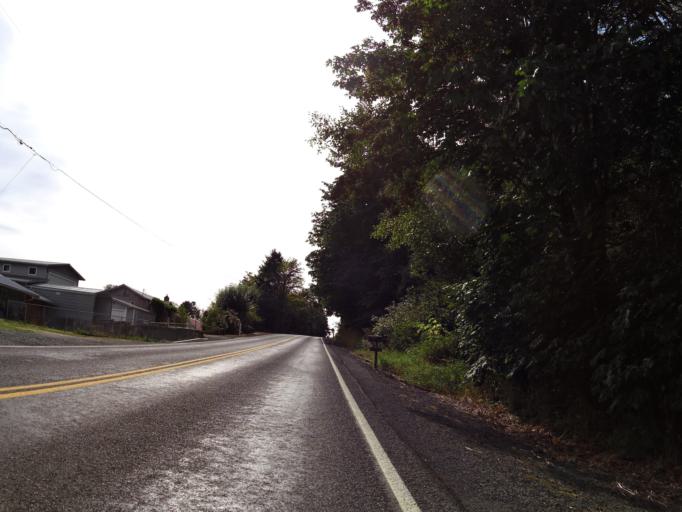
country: US
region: Washington
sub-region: Lewis County
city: Chehalis
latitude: 46.6304
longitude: -122.9687
